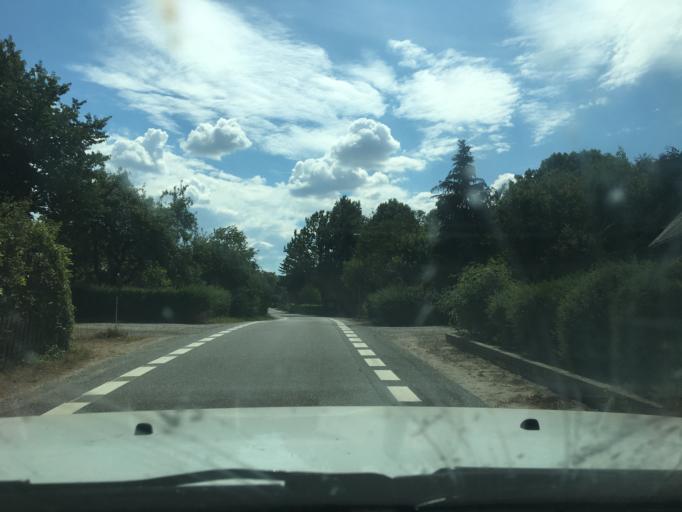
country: DK
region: Central Jutland
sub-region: Syddjurs Kommune
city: Hornslet
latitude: 56.3502
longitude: 10.2869
